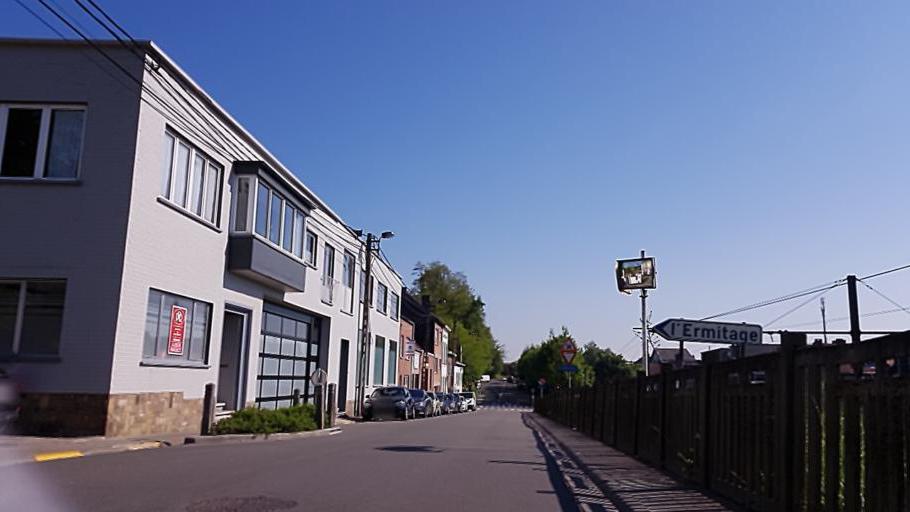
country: BE
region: Wallonia
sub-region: Province du Brabant Wallon
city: Wavre
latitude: 50.7163
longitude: 4.6049
